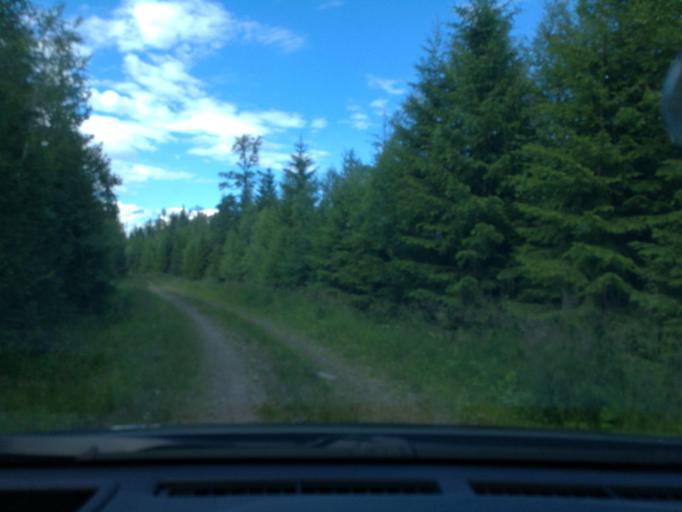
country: SE
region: Vaestmanland
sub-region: Surahammars Kommun
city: Ramnas
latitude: 59.7966
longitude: 16.2962
